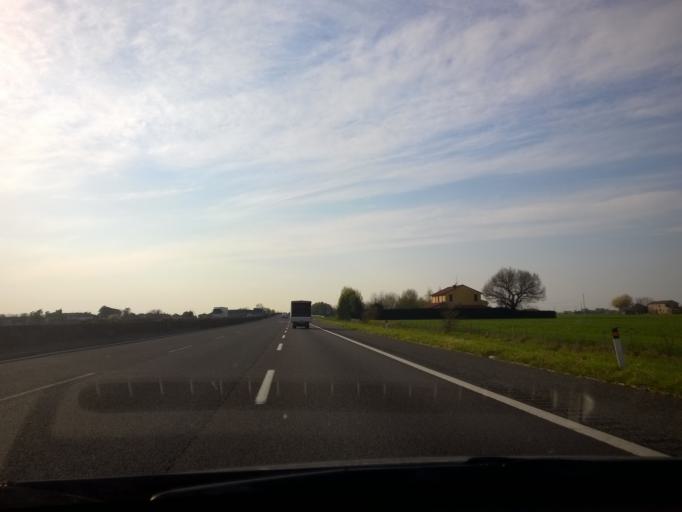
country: IT
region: Emilia-Romagna
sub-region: Forli-Cesena
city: Santa Maria Nuova
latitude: 44.2056
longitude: 12.1988
